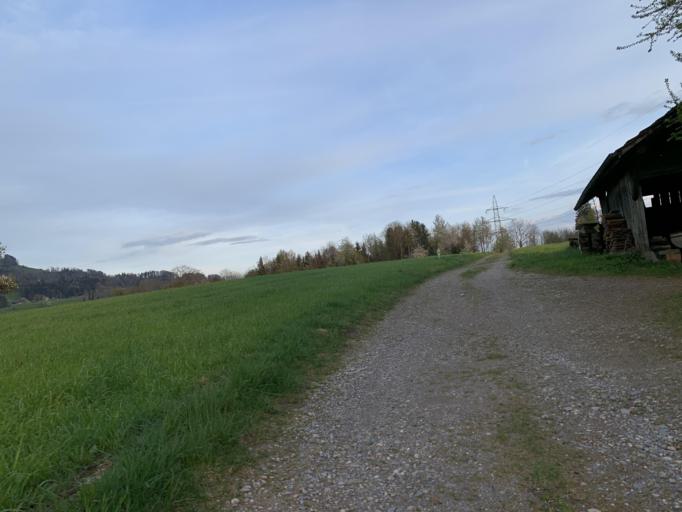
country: CH
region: Zurich
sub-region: Bezirk Hinwil
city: Durnten
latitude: 47.2828
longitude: 8.8459
